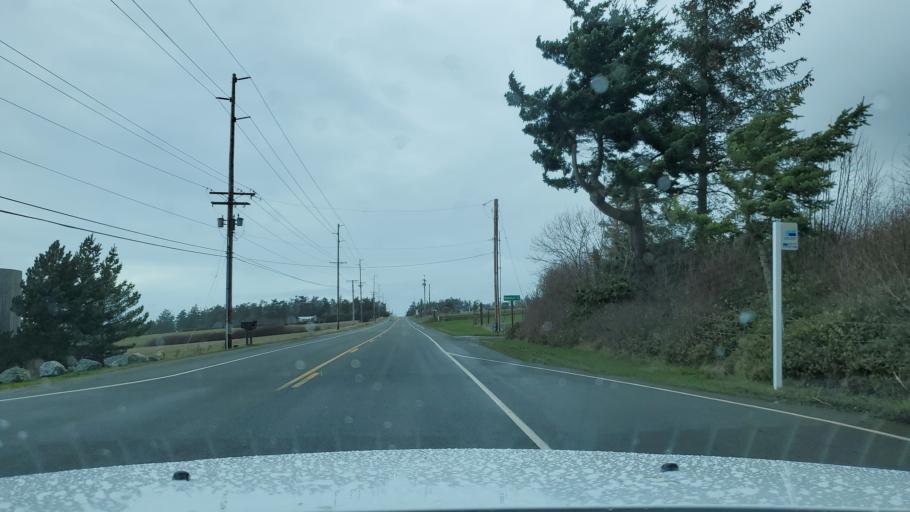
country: US
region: Washington
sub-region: Island County
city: Coupeville
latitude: 48.2387
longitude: -122.7517
